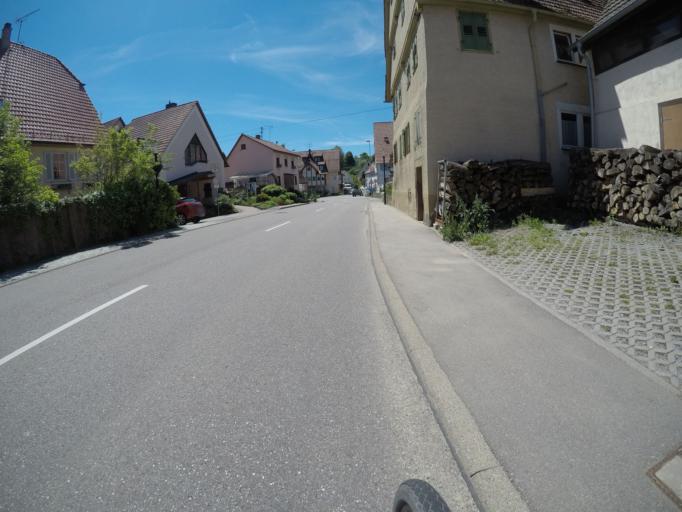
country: DE
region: Baden-Wuerttemberg
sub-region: Karlsruhe Region
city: Heimsheim
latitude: 48.7898
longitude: 8.8338
